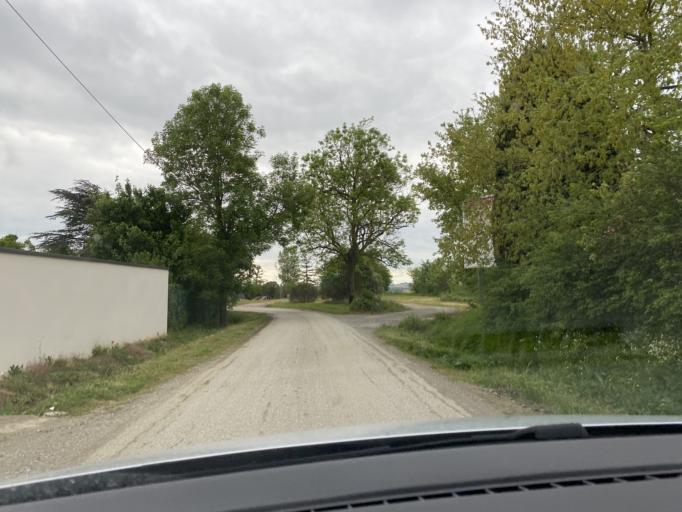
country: FR
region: Midi-Pyrenees
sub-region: Departement de la Haute-Garonne
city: Nailloux
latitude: 43.3615
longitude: 1.6289
